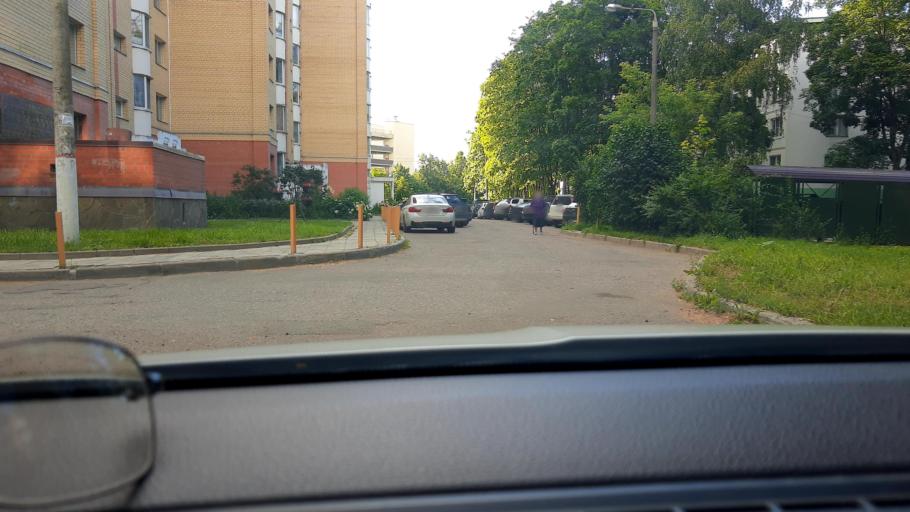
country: RU
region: Moskovskaya
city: Povedniki
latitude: 55.9746
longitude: 37.6083
